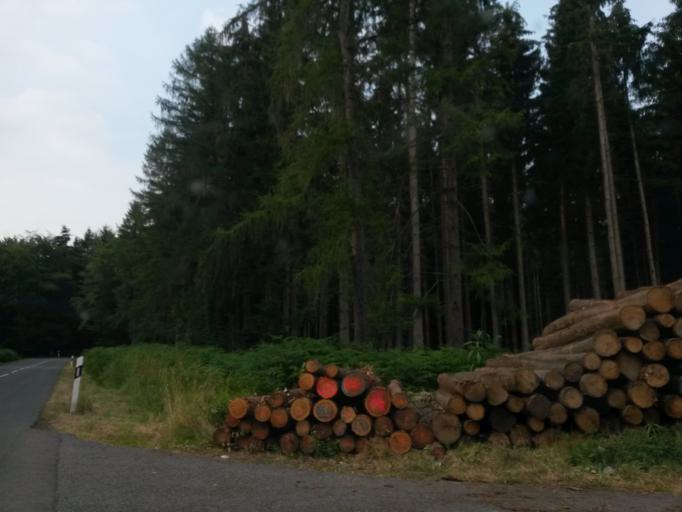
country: DE
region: North Rhine-Westphalia
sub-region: Regierungsbezirk Koln
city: Hennef
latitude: 50.7868
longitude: 7.3019
